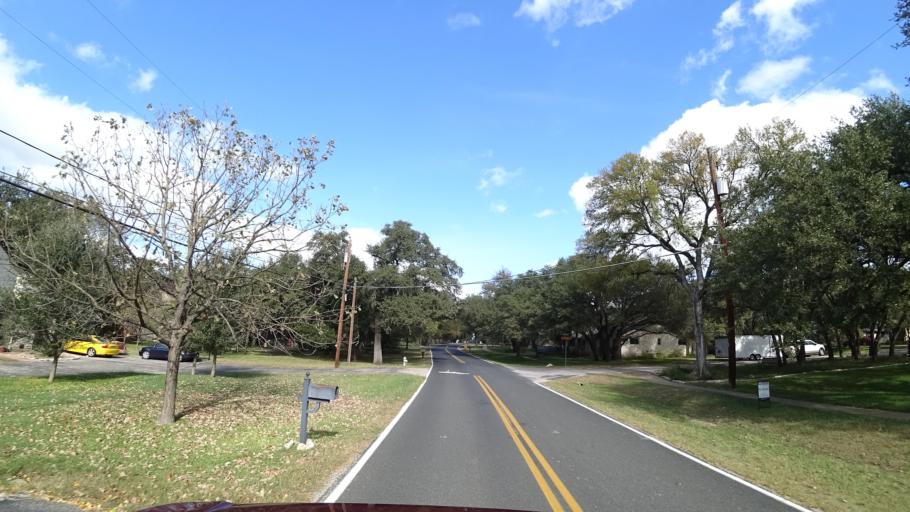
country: US
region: Texas
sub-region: Williamson County
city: Jollyville
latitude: 30.4158
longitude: -97.7817
